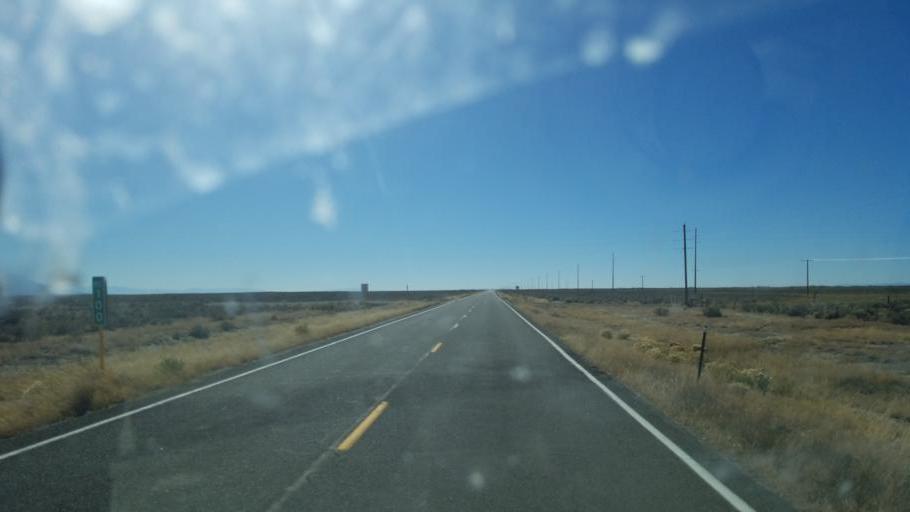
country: US
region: Colorado
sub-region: Saguache County
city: Center
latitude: 37.9204
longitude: -105.8997
